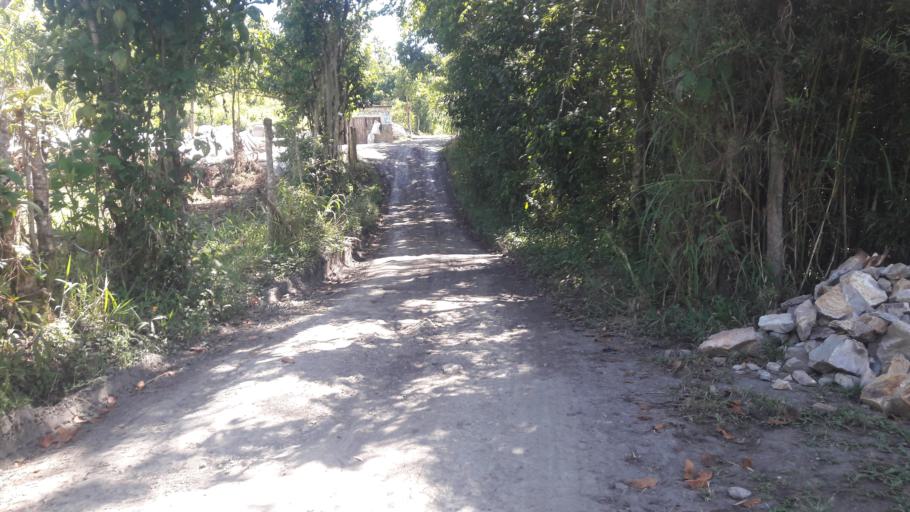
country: CO
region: Cundinamarca
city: Tenza
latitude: 5.0807
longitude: -73.4100
